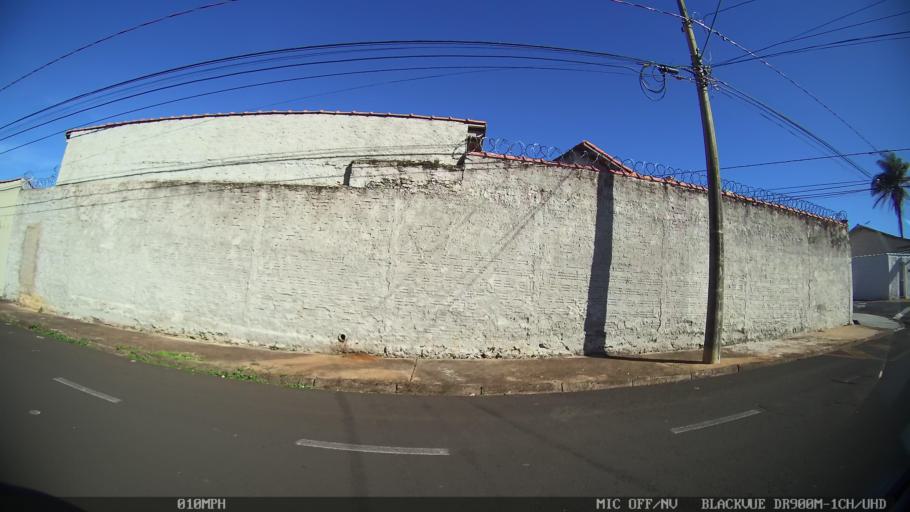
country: BR
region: Sao Paulo
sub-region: Franca
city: Franca
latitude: -20.5487
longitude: -47.4109
